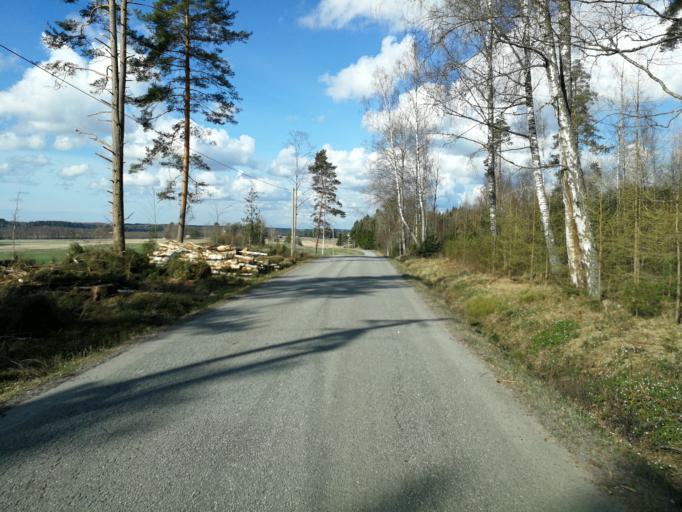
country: FI
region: Uusimaa
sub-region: Helsinki
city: Lohja
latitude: 60.1542
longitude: 24.1054
